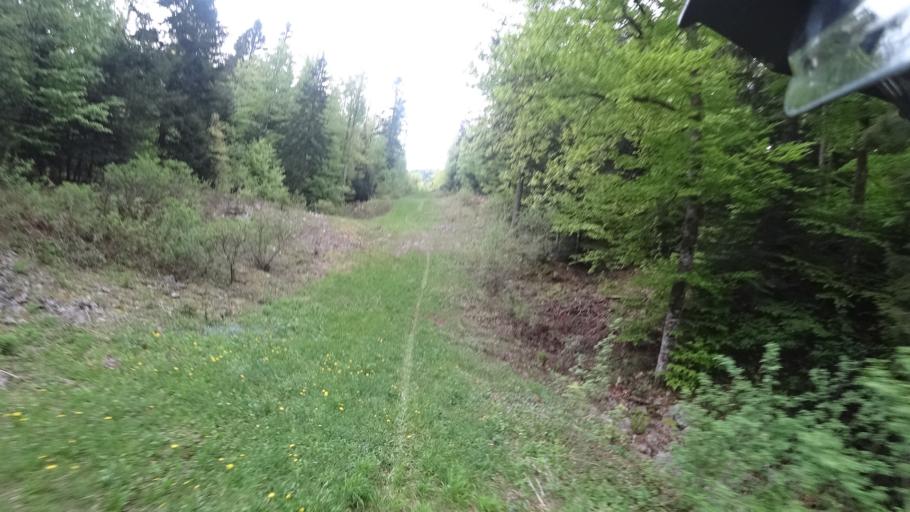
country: HR
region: Karlovacka
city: Plaski
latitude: 44.9284
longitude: 15.4246
